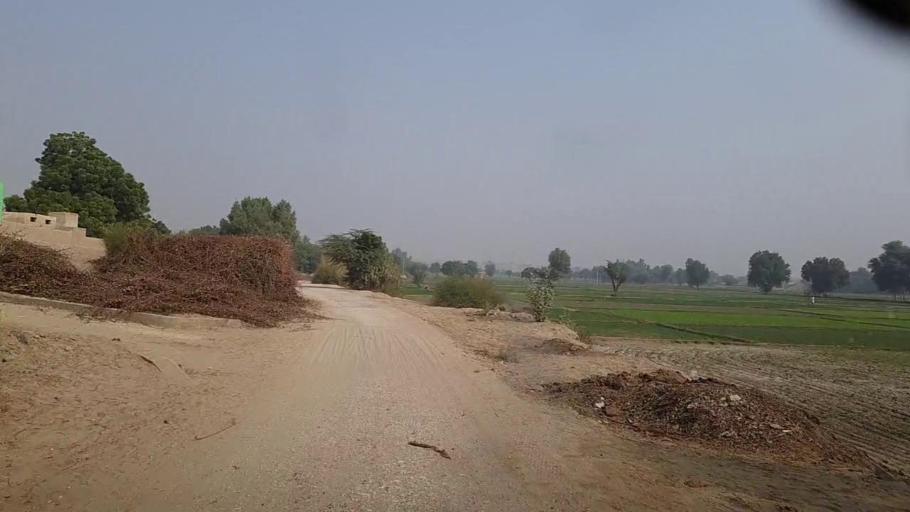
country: PK
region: Sindh
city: Bozdar
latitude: 27.0578
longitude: 68.6603
